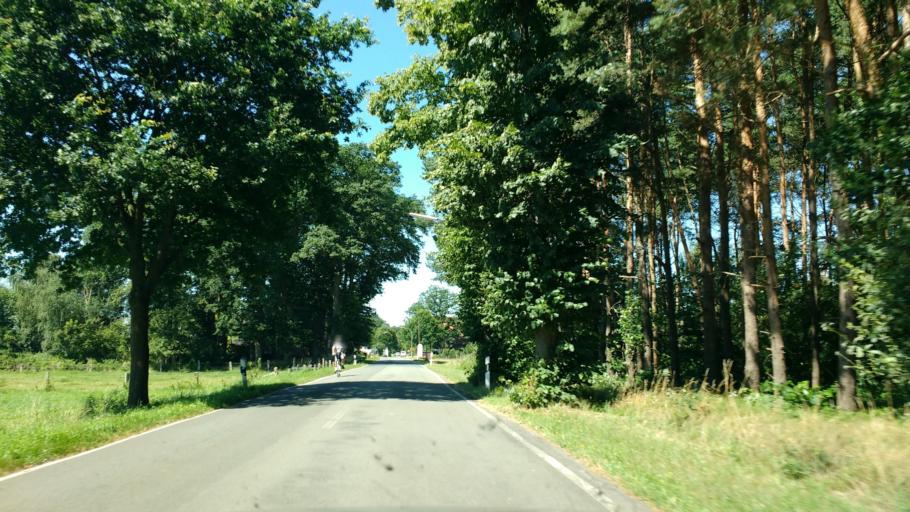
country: DE
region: North Rhine-Westphalia
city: Geseke
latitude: 51.7083
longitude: 8.4459
